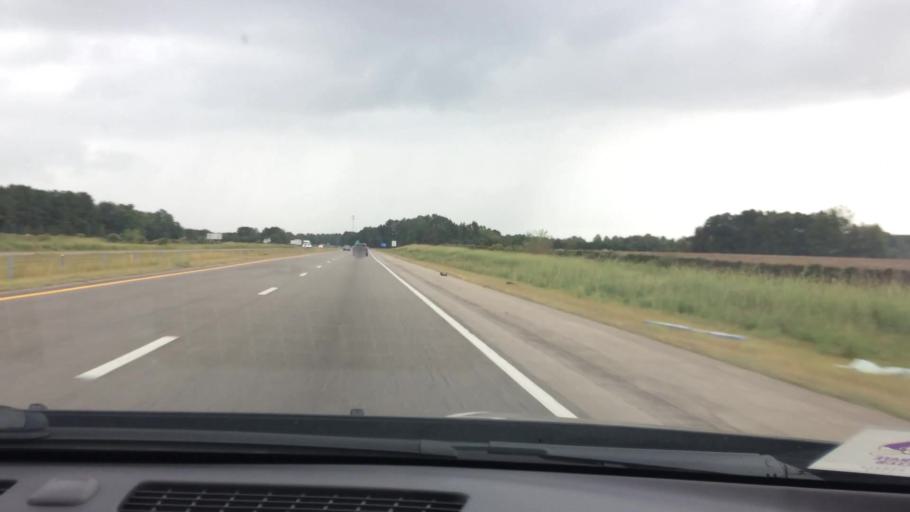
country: US
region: North Carolina
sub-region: Wilson County
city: Lucama
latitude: 35.7217
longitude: -78.0064
